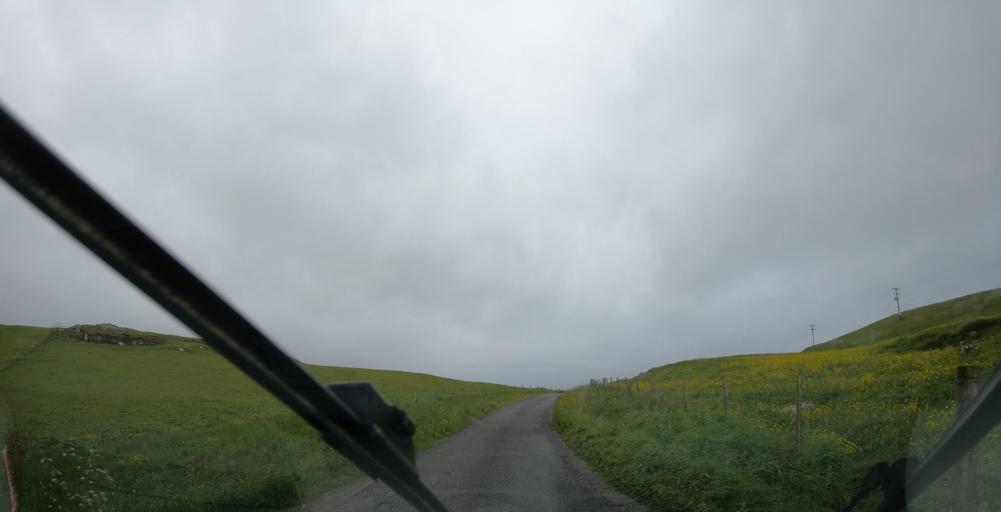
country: GB
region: Scotland
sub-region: Eilean Siar
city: Barra
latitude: 57.0340
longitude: -7.4309
